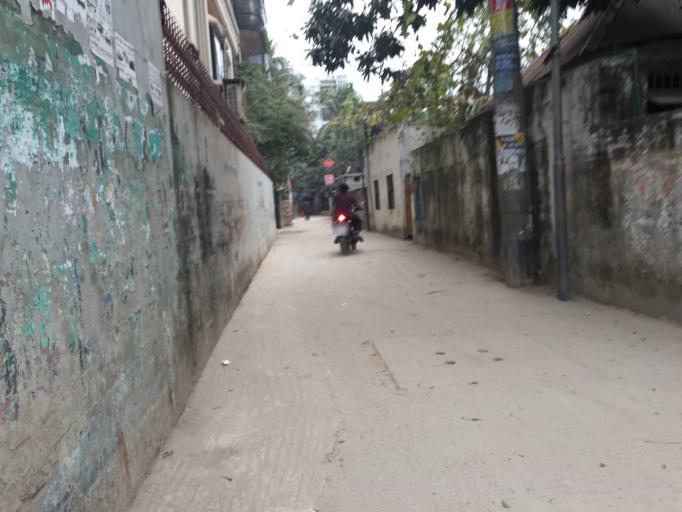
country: BD
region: Dhaka
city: Azimpur
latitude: 23.7888
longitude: 90.3577
